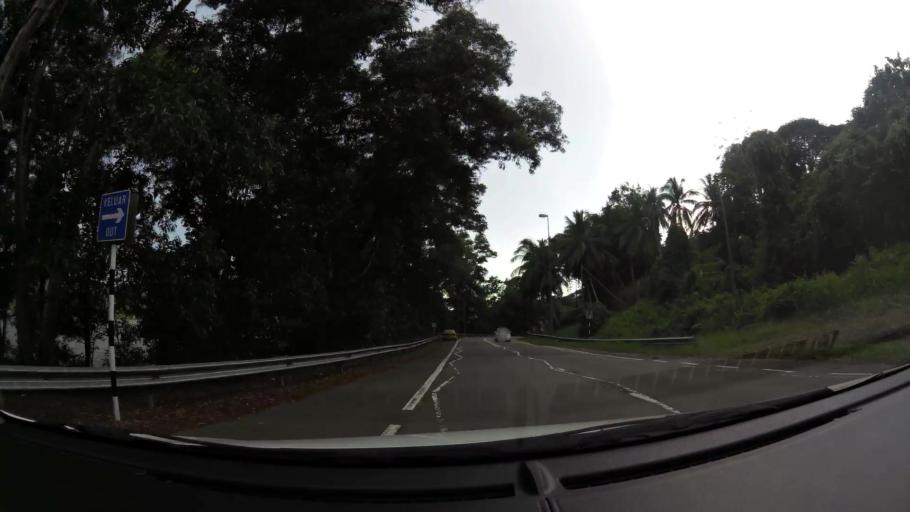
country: BN
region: Brunei and Muara
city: Bandar Seri Begawan
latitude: 4.8951
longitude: 114.9831
